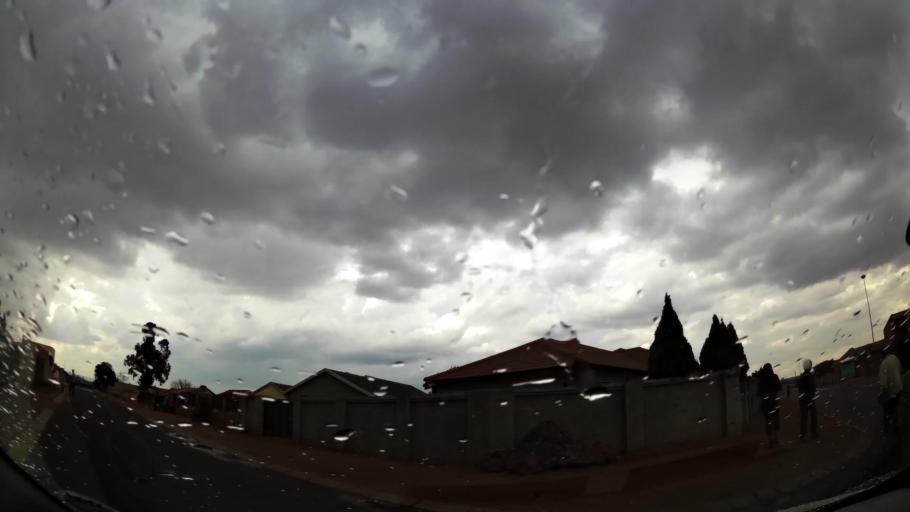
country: ZA
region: Gauteng
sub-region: Ekurhuleni Metropolitan Municipality
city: Germiston
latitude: -26.3630
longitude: 28.1648
